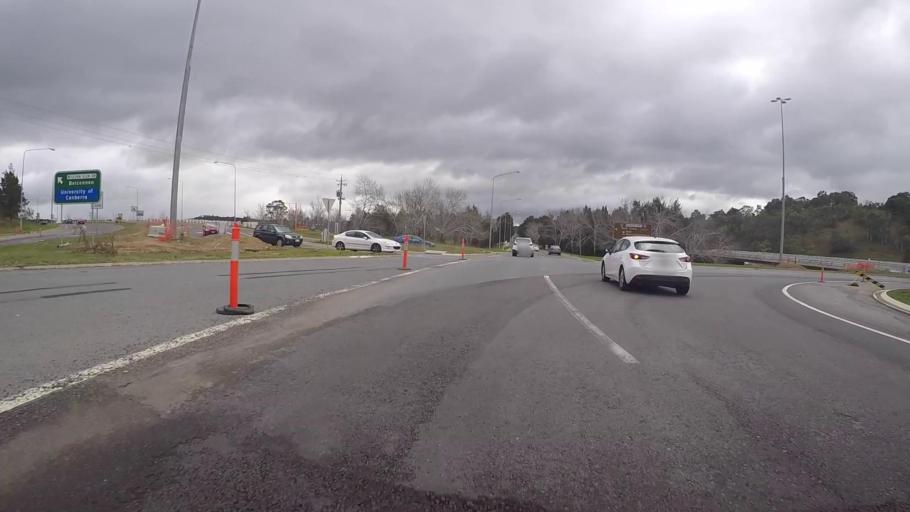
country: AU
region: Australian Capital Territory
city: Belconnen
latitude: -35.2017
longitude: 149.0945
